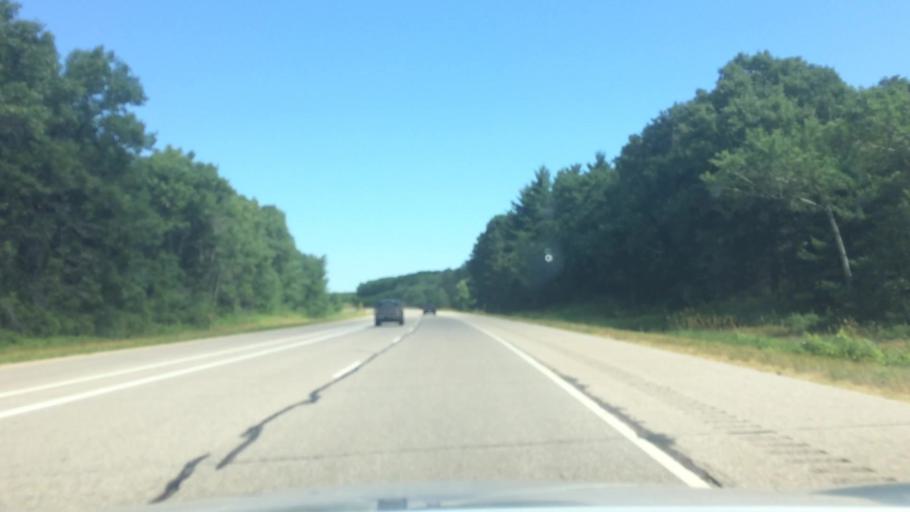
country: US
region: Wisconsin
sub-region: Marquette County
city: Westfield
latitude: 44.0799
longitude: -89.5330
